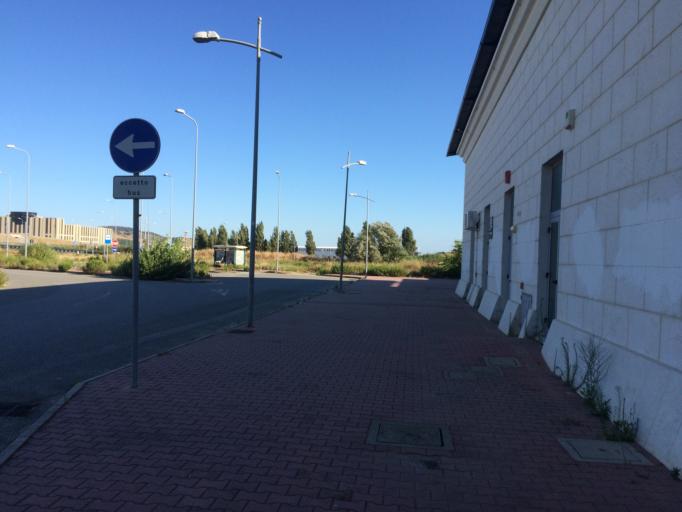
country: IT
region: Calabria
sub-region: Provincia di Catanzaro
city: Catanzaro
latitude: 38.8656
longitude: 16.5630
